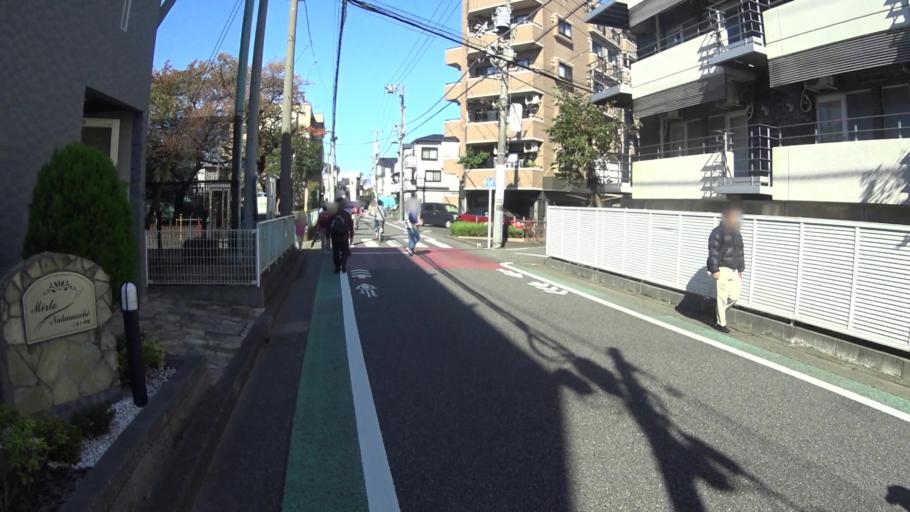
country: JP
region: Tokyo
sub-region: Machida-shi
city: Machida
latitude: 35.5528
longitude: 139.4483
